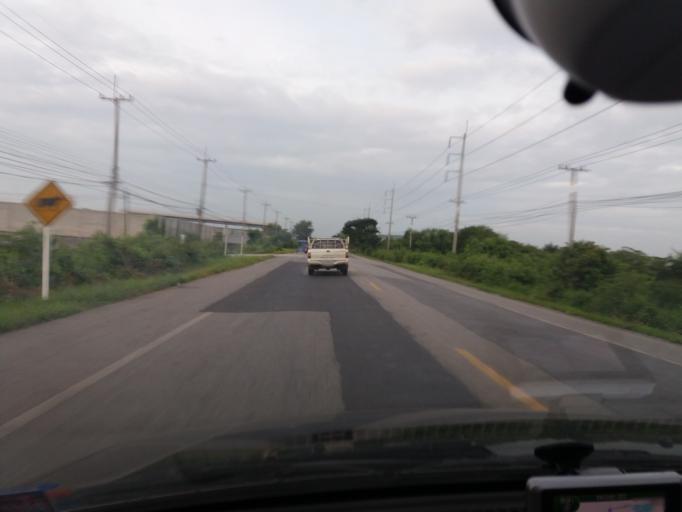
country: TH
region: Suphan Buri
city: U Thong
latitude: 14.4140
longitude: 99.9027
